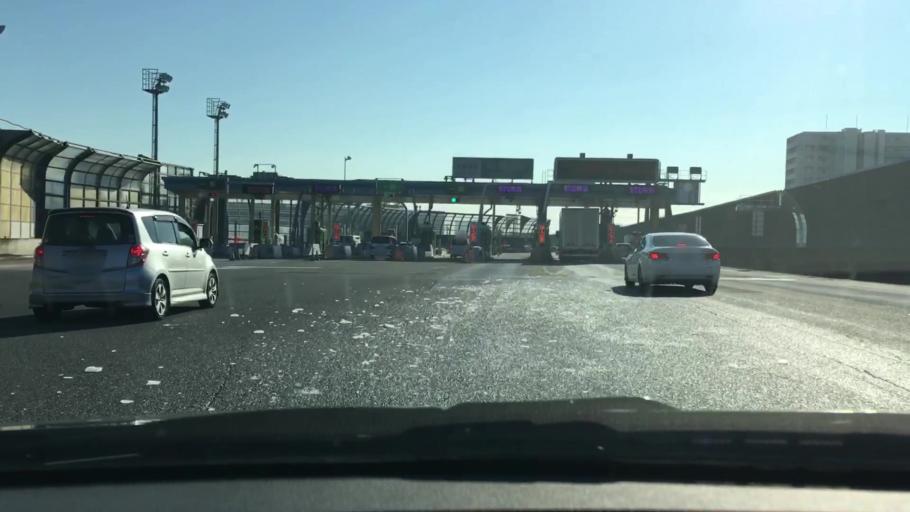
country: JP
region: Chiba
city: Funabashi
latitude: 35.6966
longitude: 139.9737
